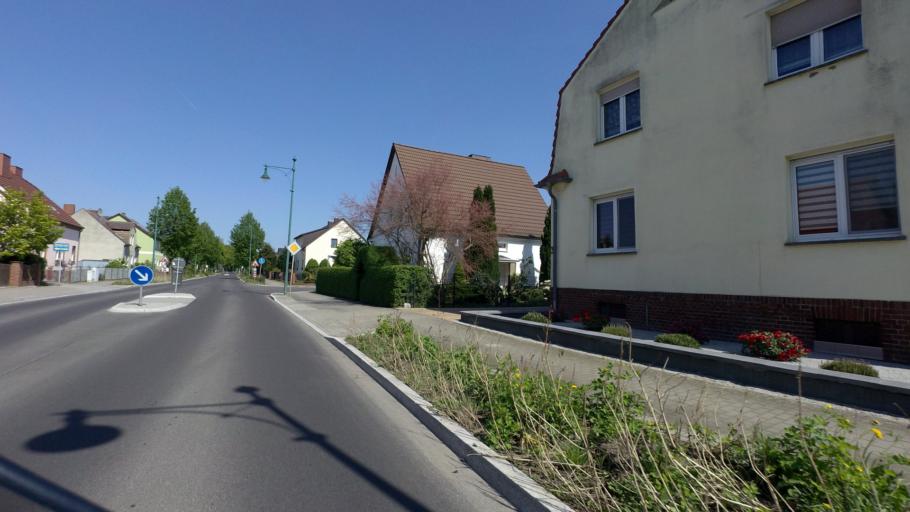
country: DE
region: Brandenburg
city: Beeskow
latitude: 52.1713
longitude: 14.2663
